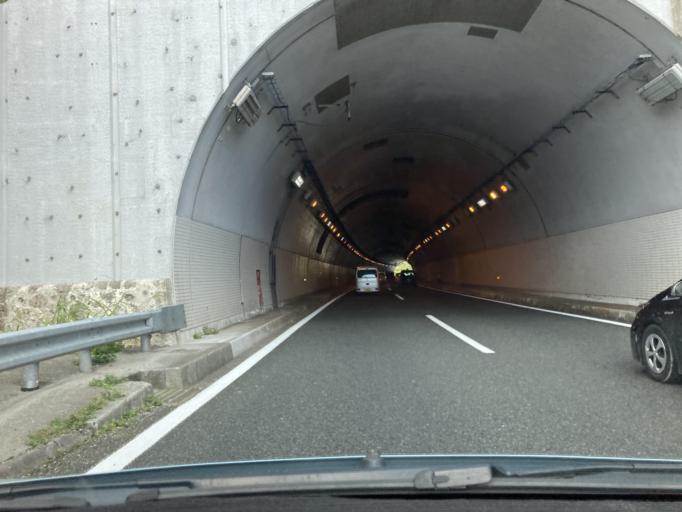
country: JP
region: Okinawa
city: Chatan
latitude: 26.3067
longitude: 127.7890
